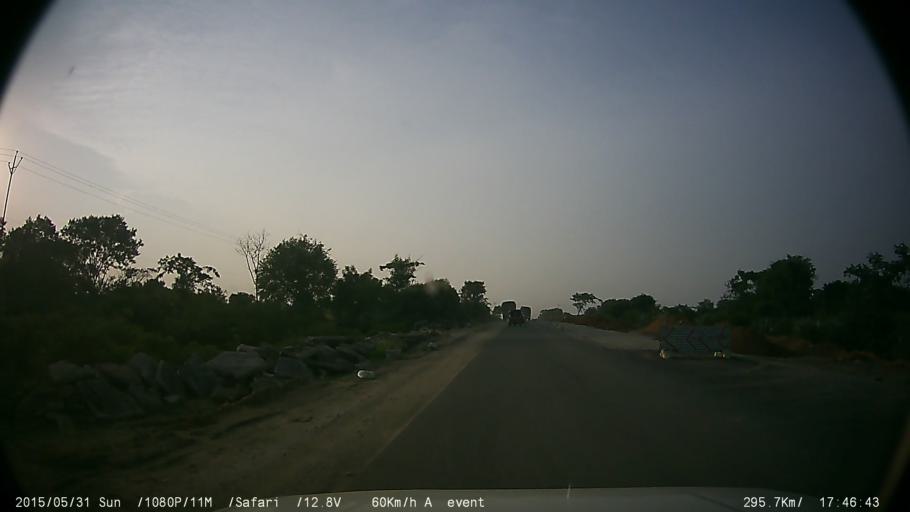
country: IN
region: Karnataka
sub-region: Chamrajnagar
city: Gundlupet
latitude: 11.9594
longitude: 76.6705
